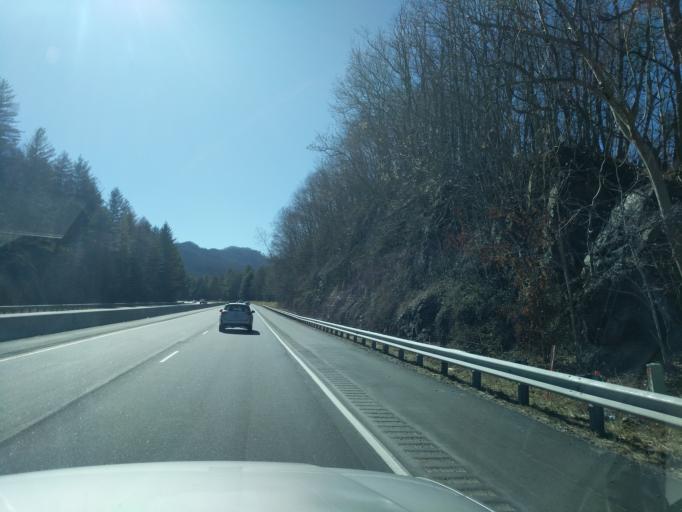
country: US
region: North Carolina
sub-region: Jackson County
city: Cullowhee
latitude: 35.4061
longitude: -83.1242
